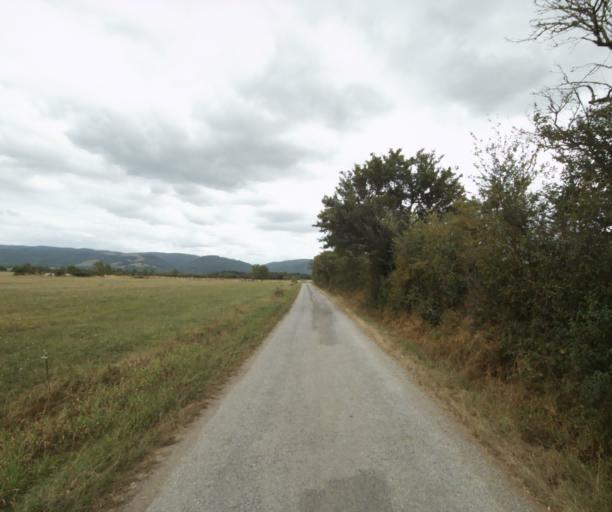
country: FR
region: Midi-Pyrenees
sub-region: Departement de la Haute-Garonne
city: Revel
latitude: 43.4780
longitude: 2.0327
